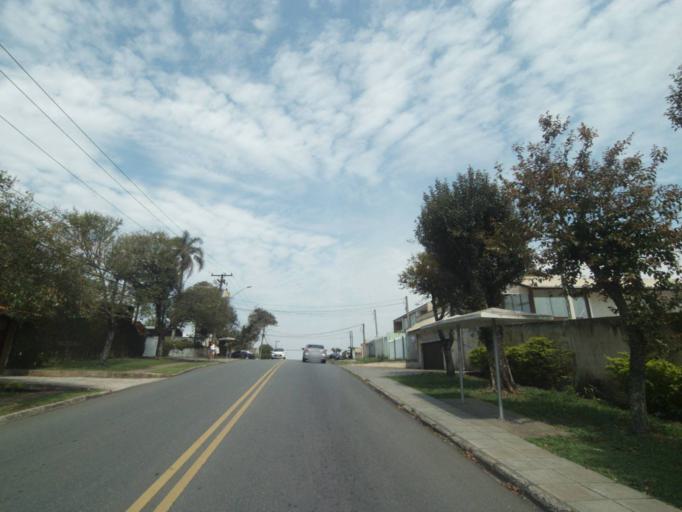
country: BR
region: Parana
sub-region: Pinhais
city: Pinhais
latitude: -25.4250
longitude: -49.2058
